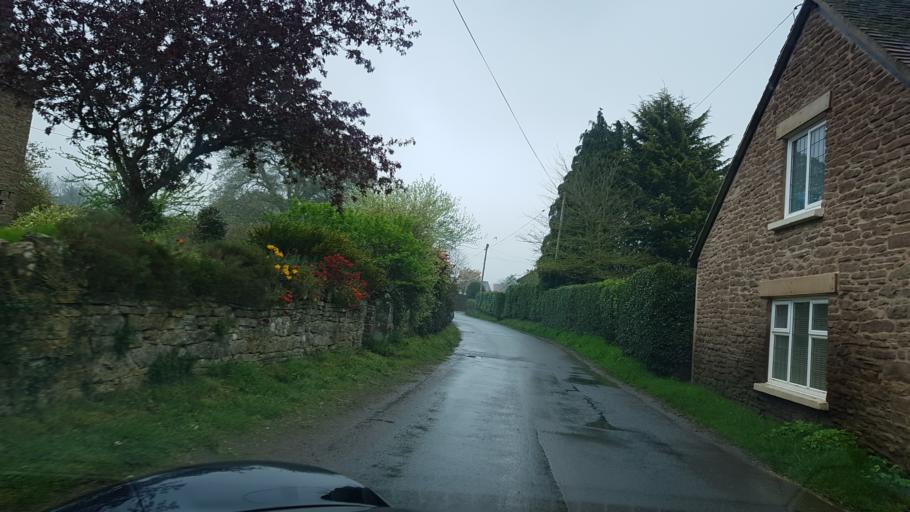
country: GB
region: England
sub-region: Herefordshire
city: Brockhampton
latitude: 51.9812
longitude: -2.6014
